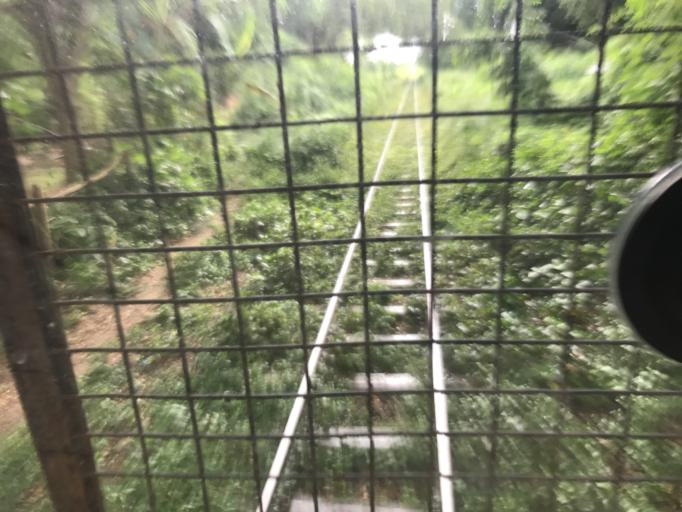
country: MM
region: Bago
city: Paungde
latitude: 18.6269
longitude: 95.4259
